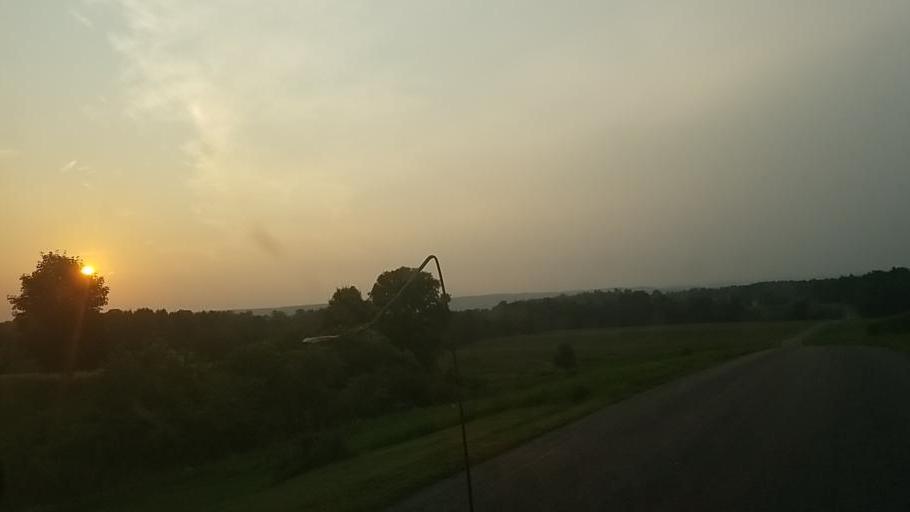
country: US
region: New York
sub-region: Montgomery County
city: Fonda
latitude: 42.9051
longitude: -74.3928
